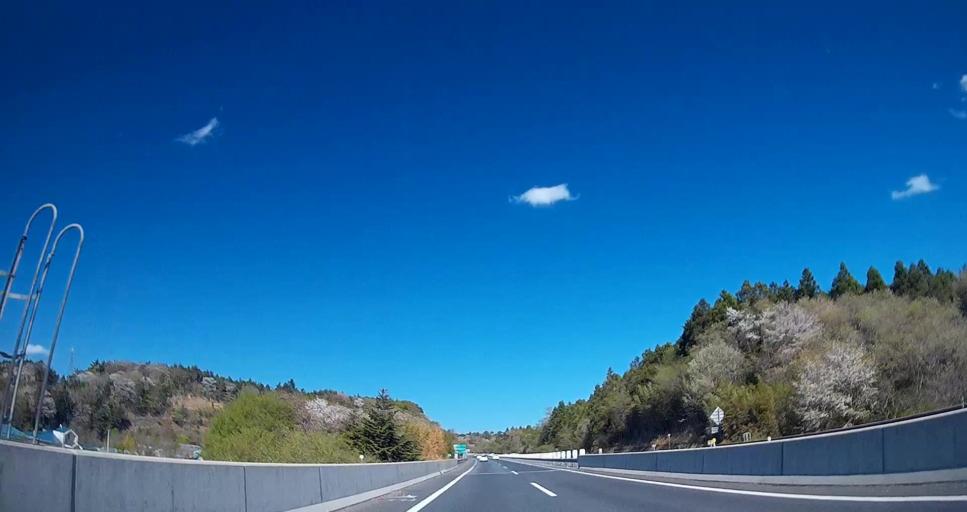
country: JP
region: Miyagi
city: Yamoto
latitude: 38.4249
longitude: 141.1601
